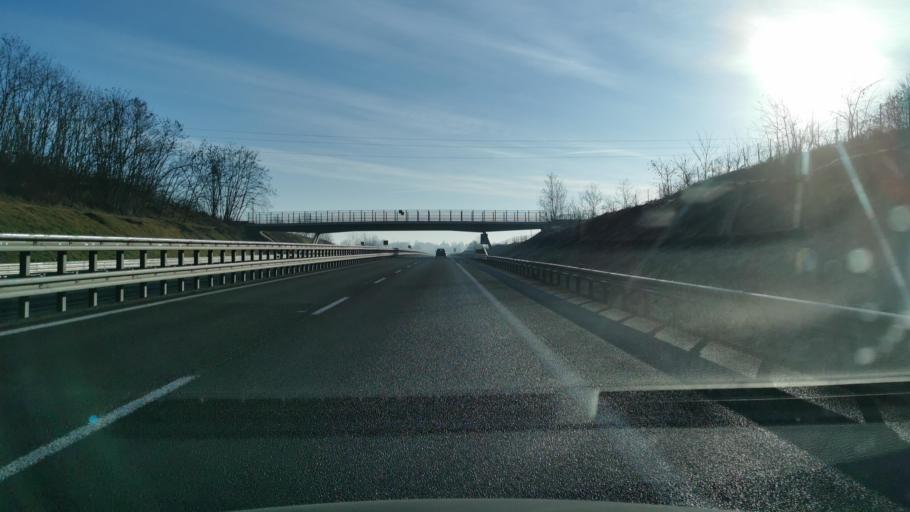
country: IT
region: Piedmont
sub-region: Provincia di Asti
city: Baldichieri d'Asti
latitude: 44.9016
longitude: 8.1080
